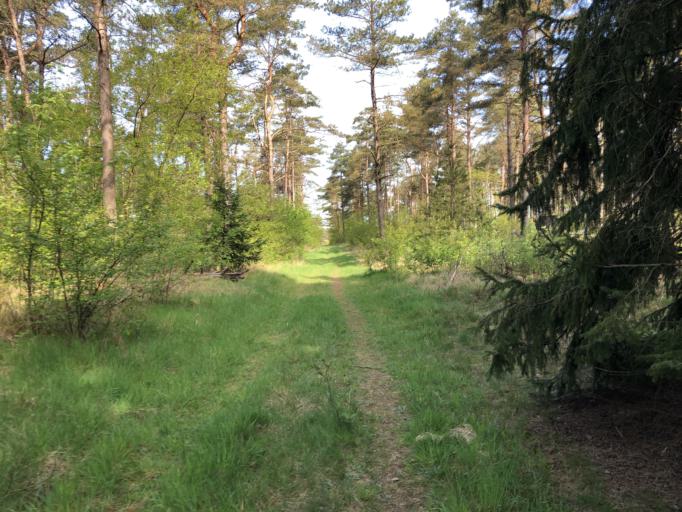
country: DK
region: Central Jutland
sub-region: Holstebro Kommune
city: Ulfborg
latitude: 56.2809
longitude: 8.4057
